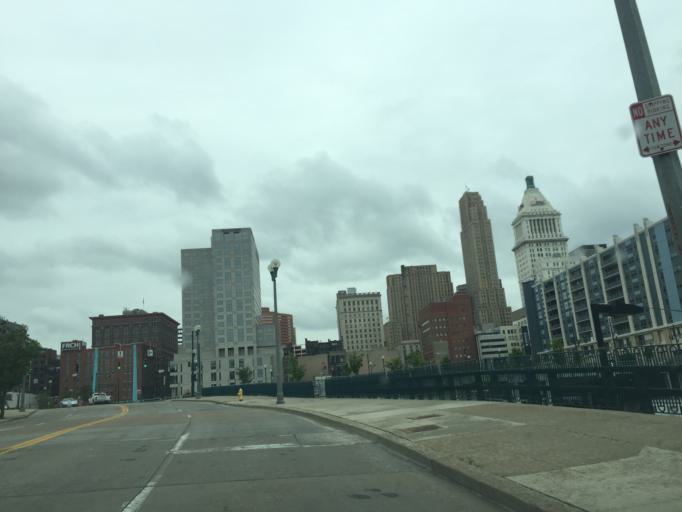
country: US
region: Kentucky
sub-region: Kenton County
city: Covington
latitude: 39.0957
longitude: -84.5141
